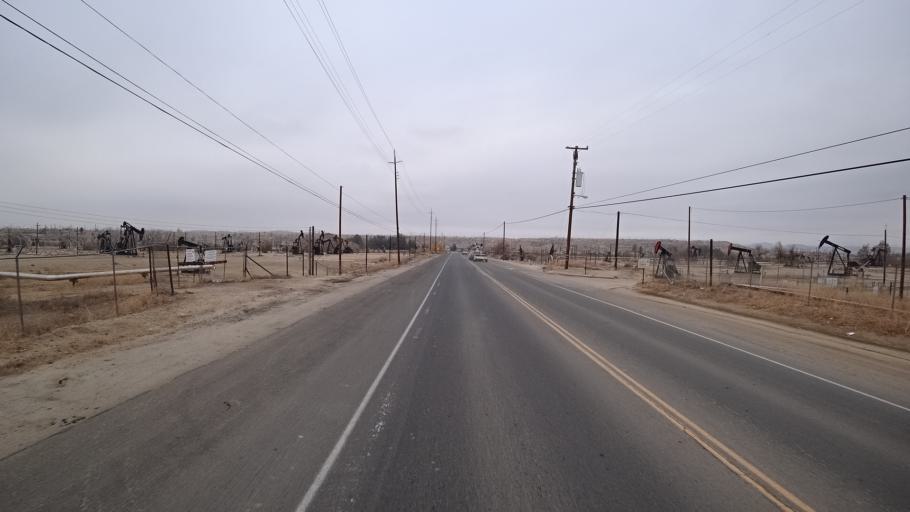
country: US
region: California
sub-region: Kern County
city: Oildale
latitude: 35.4230
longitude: -118.9678
